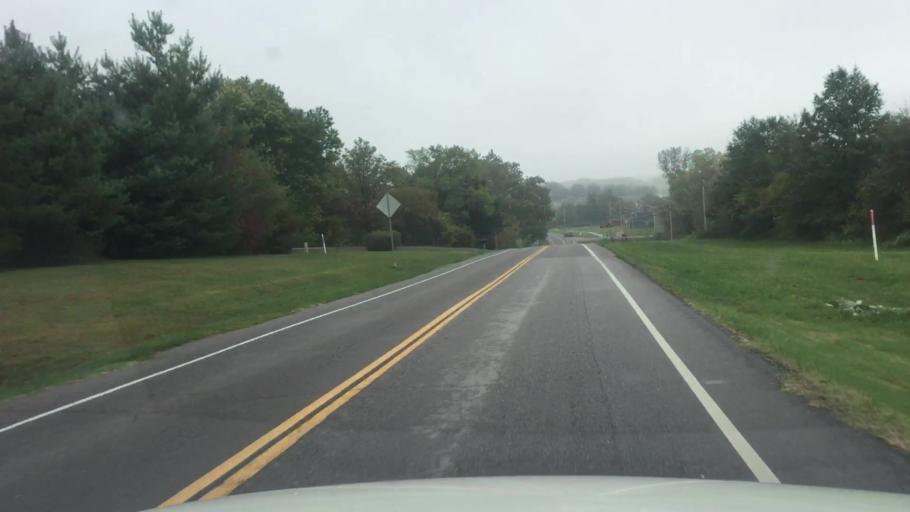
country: US
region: Missouri
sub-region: Boone County
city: Columbia
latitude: 38.8708
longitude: -92.3856
